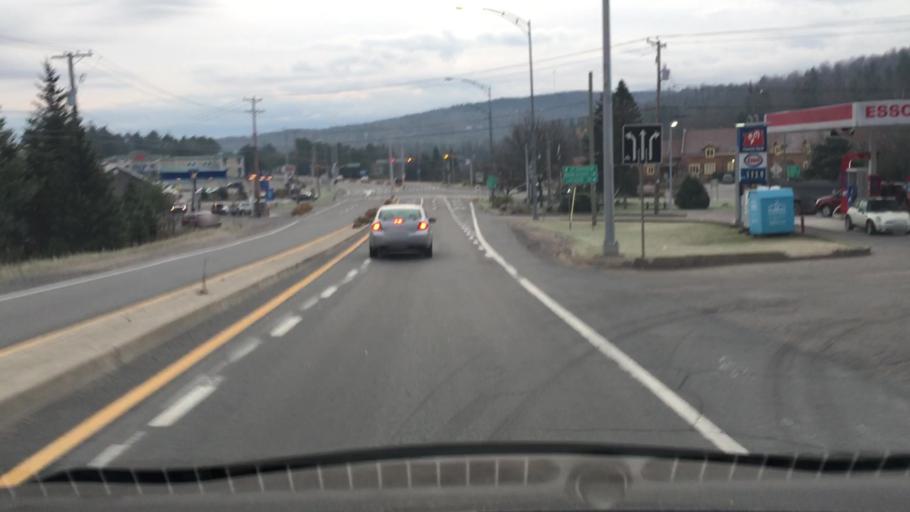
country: CA
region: Quebec
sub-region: Laurentides
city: Saint-Sauveur
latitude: 45.9046
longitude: -74.2475
